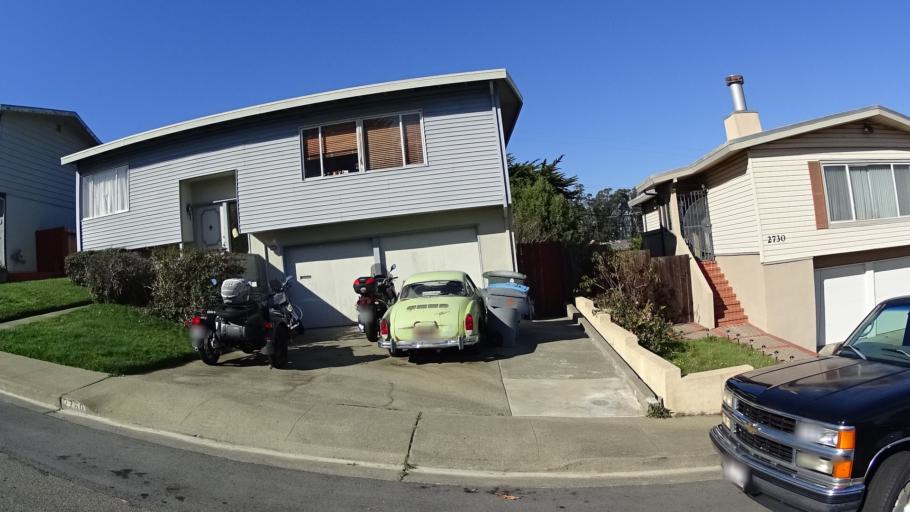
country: US
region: California
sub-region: San Mateo County
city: San Bruno
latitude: 37.6322
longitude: -122.4495
